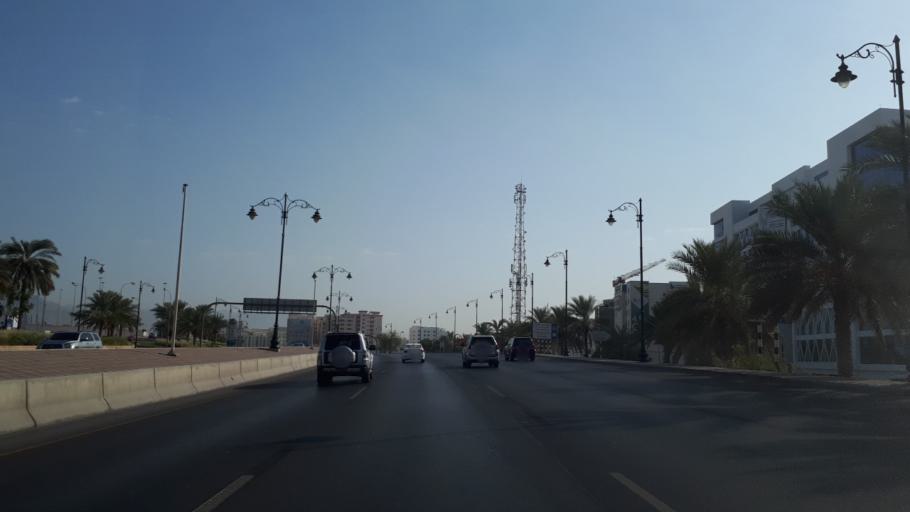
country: OM
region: Muhafazat Masqat
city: Bawshar
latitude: 23.5944
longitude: 58.4110
